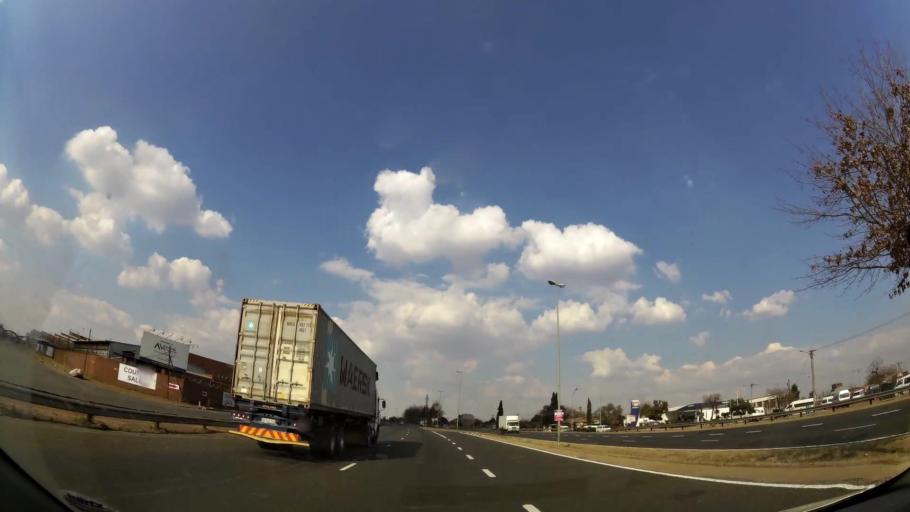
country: ZA
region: Gauteng
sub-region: Ekurhuleni Metropolitan Municipality
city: Germiston
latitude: -26.2999
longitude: 28.1812
